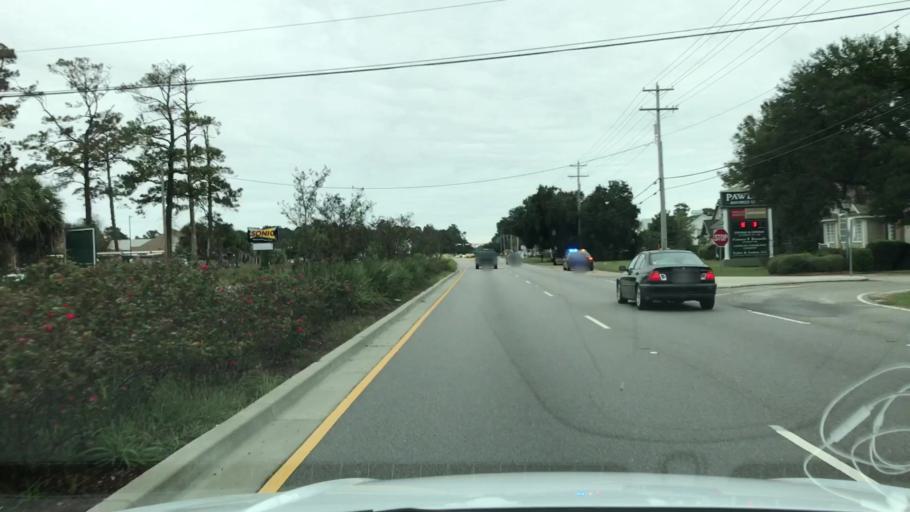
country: US
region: South Carolina
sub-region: Georgetown County
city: Murrells Inlet
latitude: 33.4471
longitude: -79.1212
